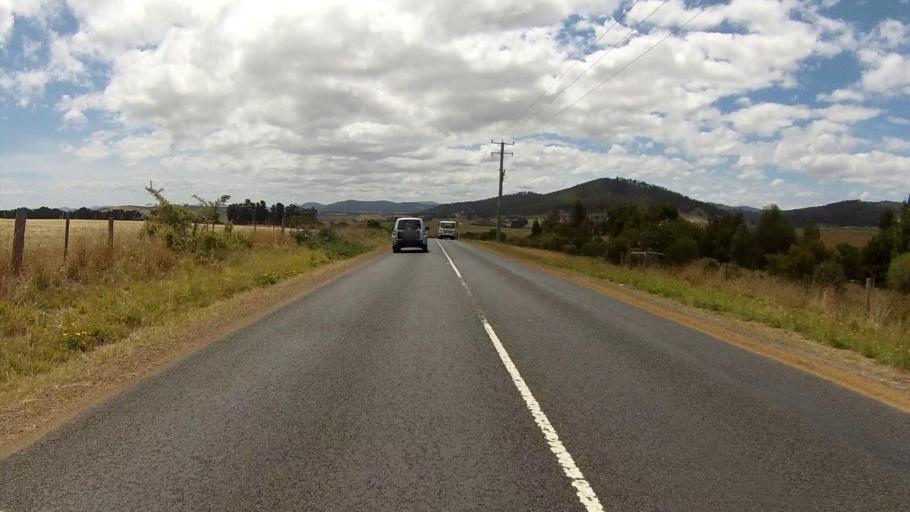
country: AU
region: Tasmania
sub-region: Sorell
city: Sorell
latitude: -42.8122
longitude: 147.6134
